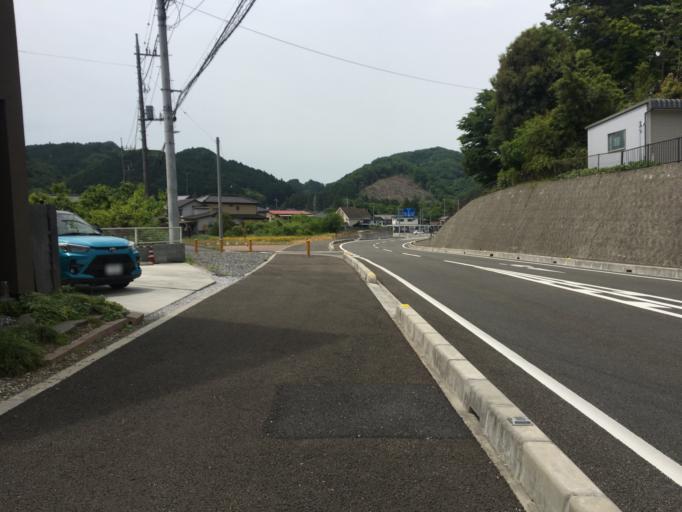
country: JP
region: Saitama
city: Hanno
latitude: 35.8582
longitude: 139.3048
